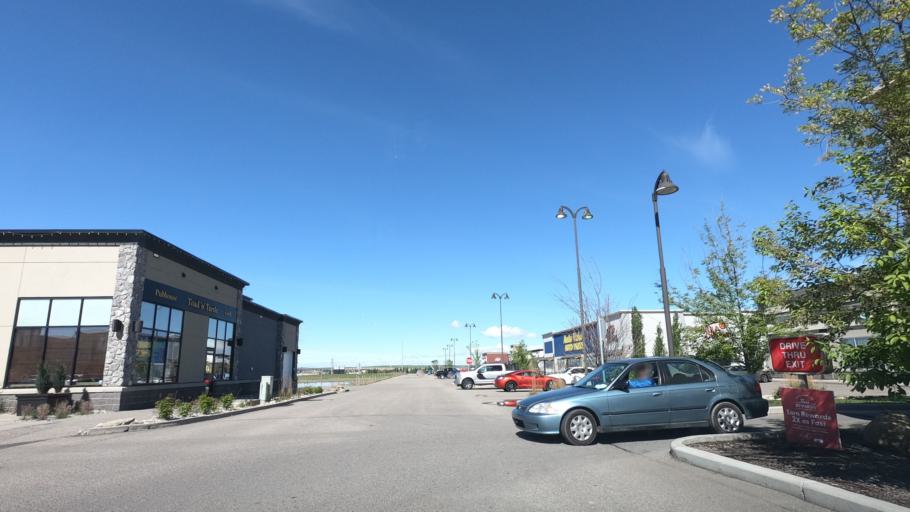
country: CA
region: Alberta
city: Airdrie
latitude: 51.2699
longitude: -113.9949
